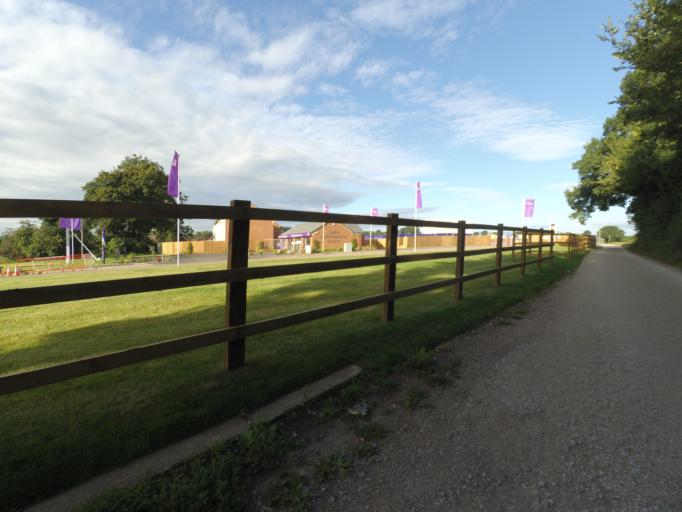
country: GB
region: England
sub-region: Staffordshire
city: Stafford
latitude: 52.8069
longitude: -2.1351
